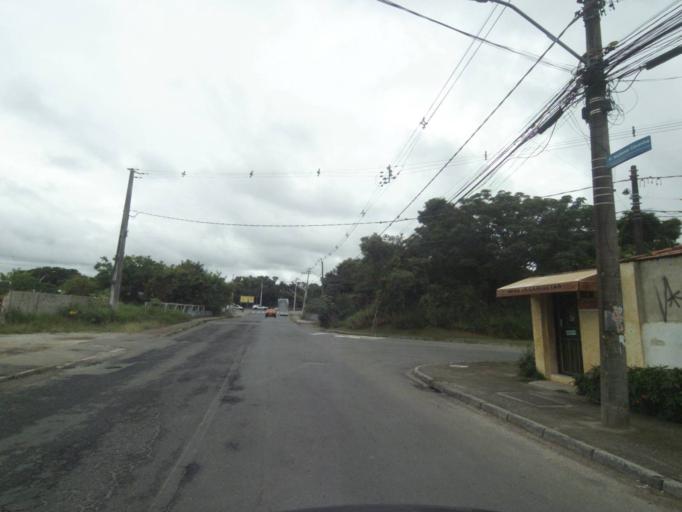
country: BR
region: Parana
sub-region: Curitiba
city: Curitiba
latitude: -25.4769
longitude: -49.3315
